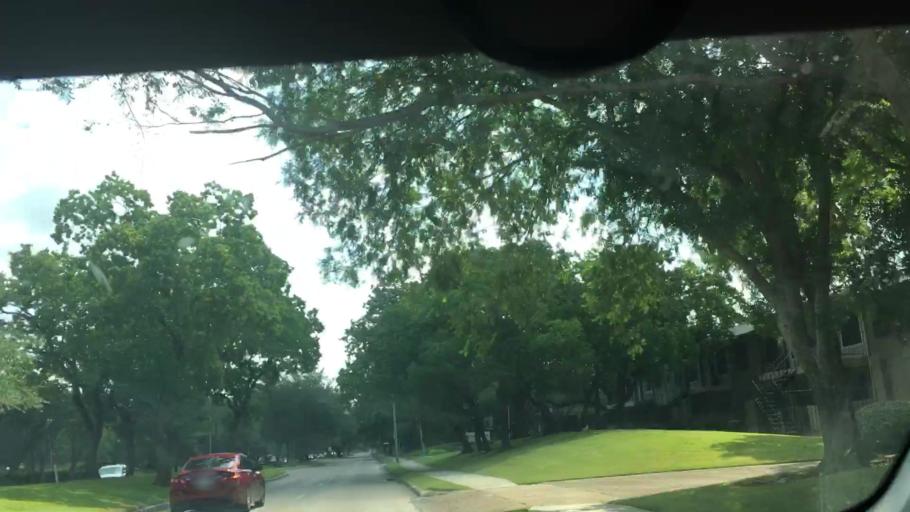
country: US
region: Texas
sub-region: Harris County
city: Bunker Hill Village
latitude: 29.7276
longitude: -95.5702
